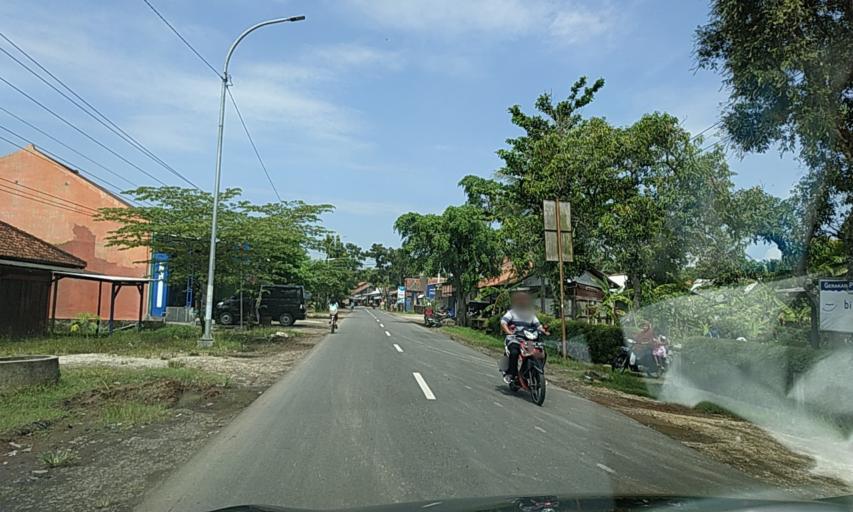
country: ID
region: Central Java
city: Mulyosari
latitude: -7.5091
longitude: 108.7846
